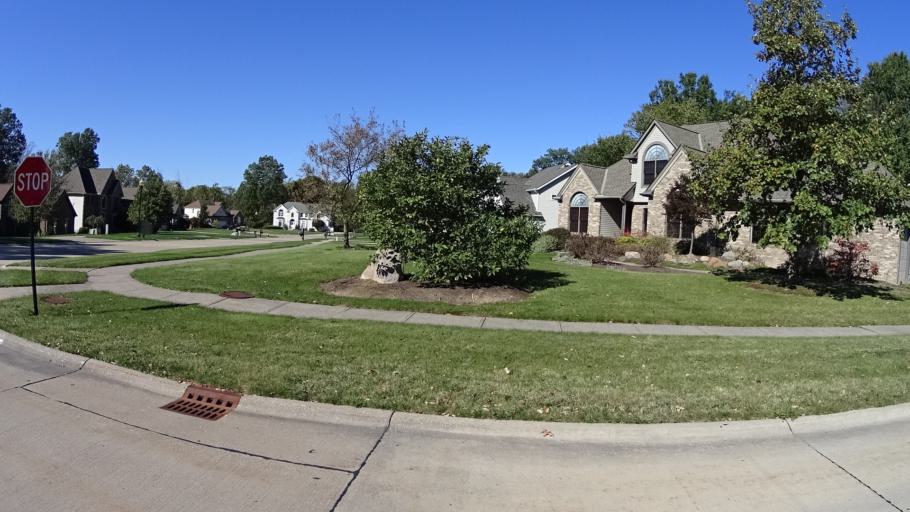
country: US
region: Ohio
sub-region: Lorain County
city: Amherst
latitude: 41.4038
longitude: -82.2331
